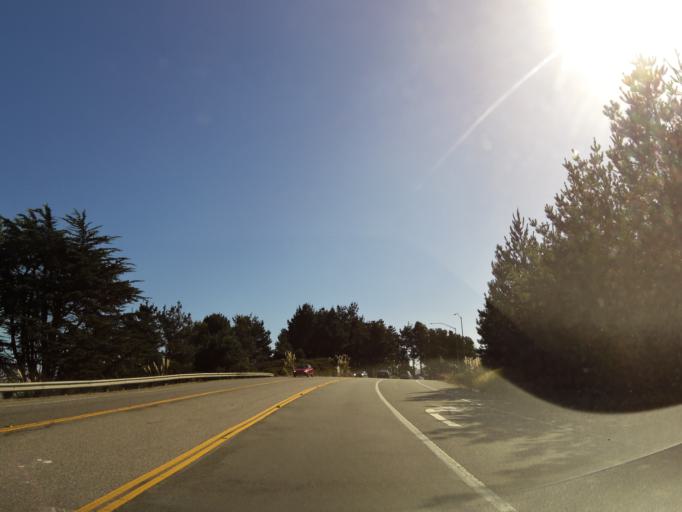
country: US
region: California
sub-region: San Mateo County
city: Colma
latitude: 37.6536
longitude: -122.4716
